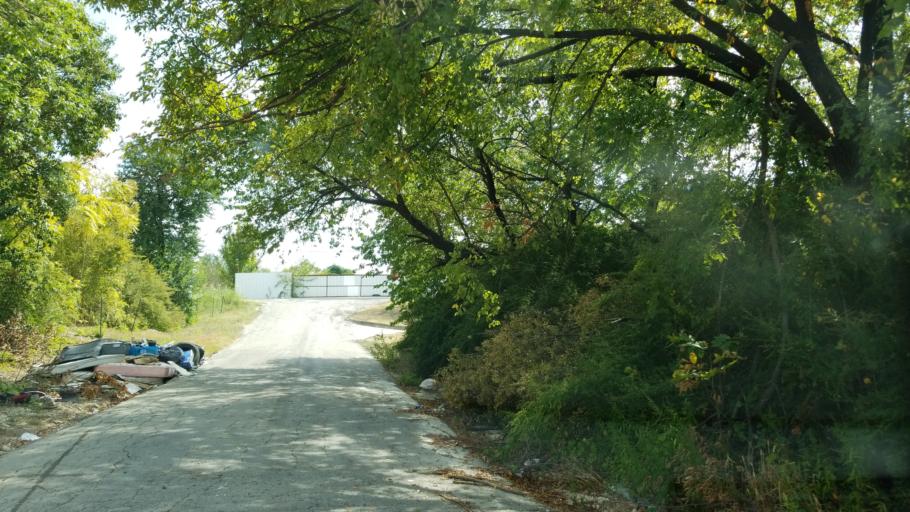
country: US
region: Texas
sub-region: Dallas County
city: Dallas
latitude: 32.7719
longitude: -96.8472
